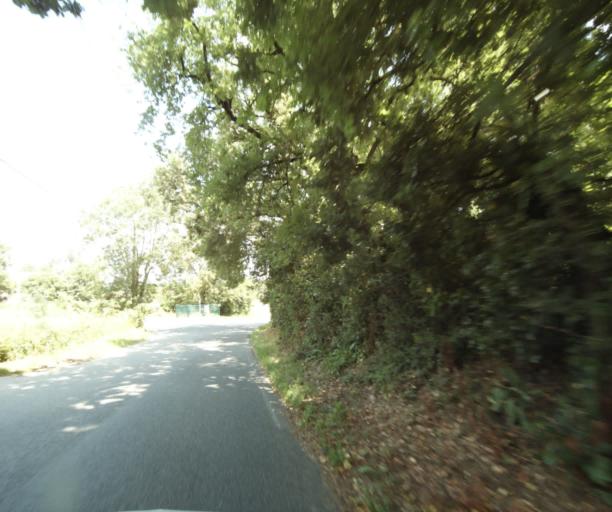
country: FR
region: Midi-Pyrenees
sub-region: Departement du Tarn-et-Garonne
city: Montauban
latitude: 44.0646
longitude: 1.3345
